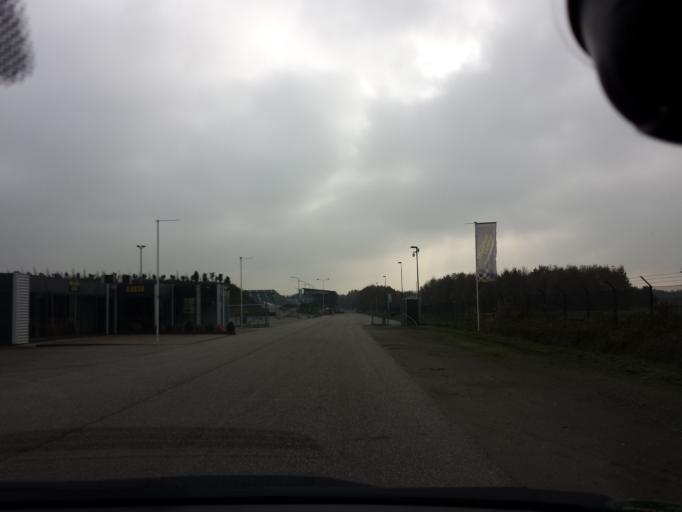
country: NL
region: North Brabant
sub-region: Gemeente Boxmeer
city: Overloon
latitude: 51.5234
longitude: 5.8752
